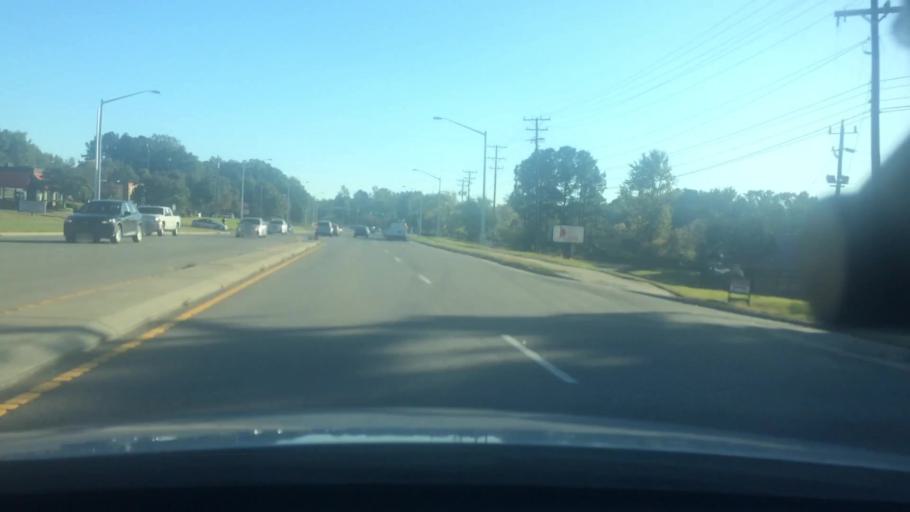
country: US
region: North Carolina
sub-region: Durham County
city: Durham
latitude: 35.9011
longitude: -78.8961
